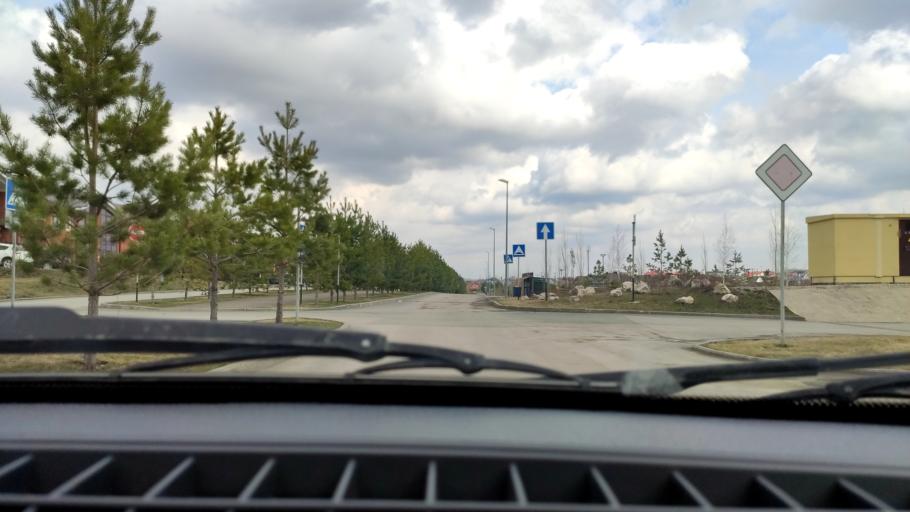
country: RU
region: Bashkortostan
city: Ufa
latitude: 54.5951
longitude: 55.9229
